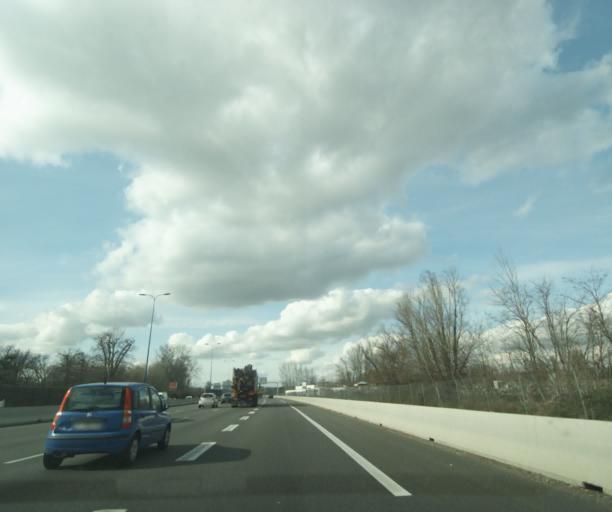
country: FR
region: Midi-Pyrenees
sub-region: Departement de la Haute-Garonne
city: Ramonville-Saint-Agne
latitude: 43.5671
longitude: 1.4825
